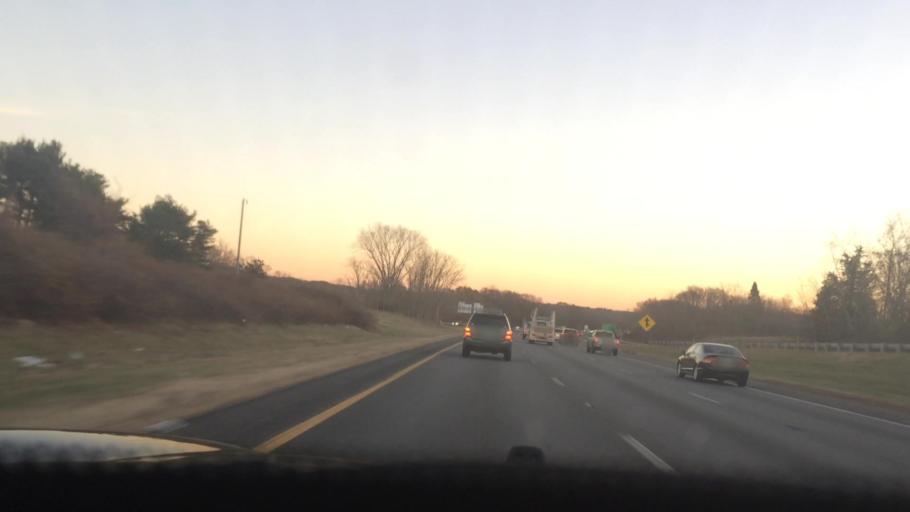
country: US
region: Massachusetts
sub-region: Essex County
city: North Andover
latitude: 42.7266
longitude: -71.1386
